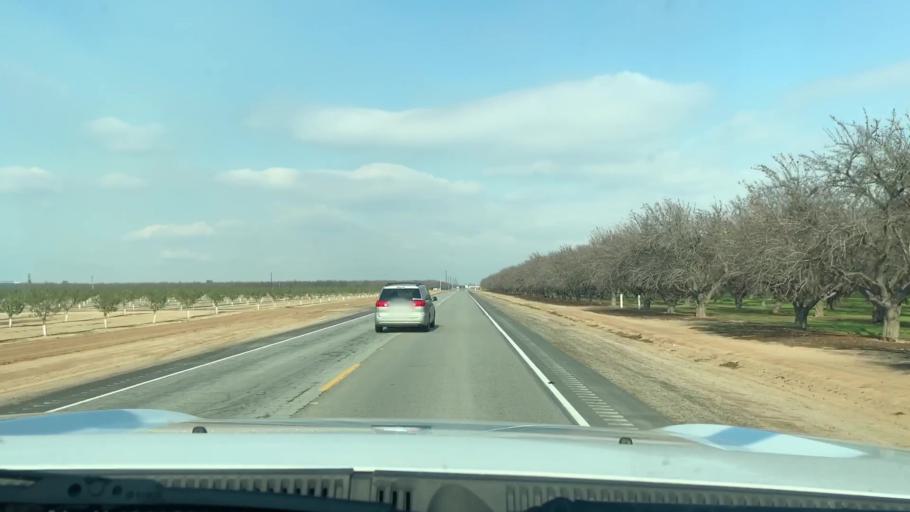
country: US
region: California
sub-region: Kern County
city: Rosedale
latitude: 35.4809
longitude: -119.1531
